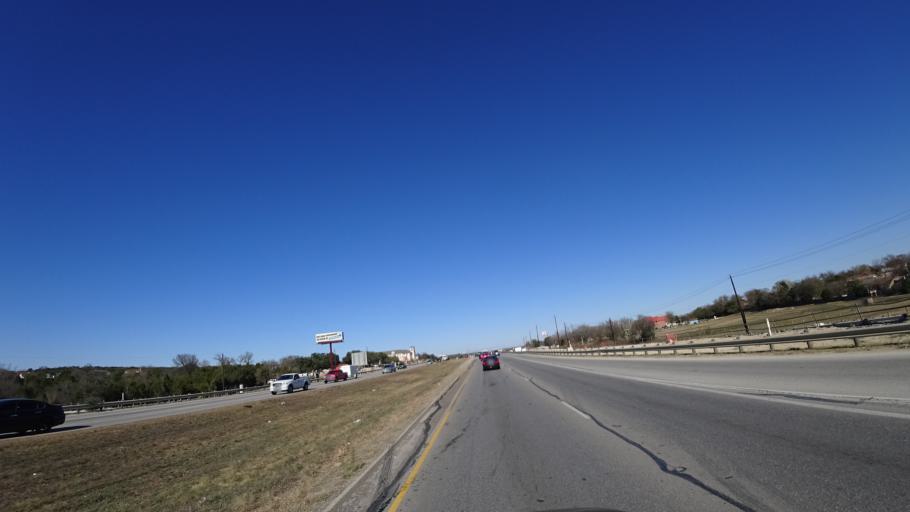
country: US
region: Texas
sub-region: Travis County
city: Austin
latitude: 30.2891
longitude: -97.6644
